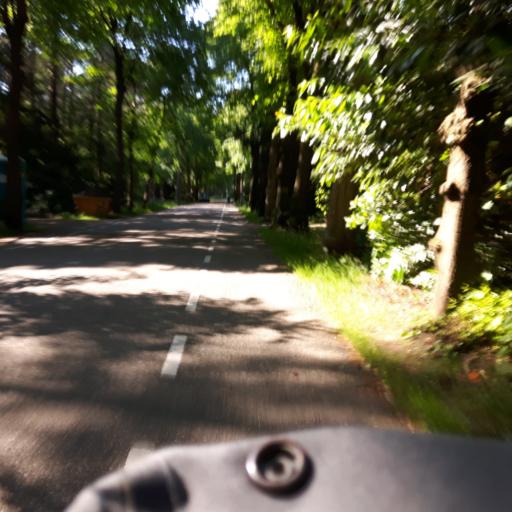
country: NL
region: Utrecht
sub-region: Gemeente Zeist
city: Zeist
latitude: 52.1291
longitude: 5.2399
